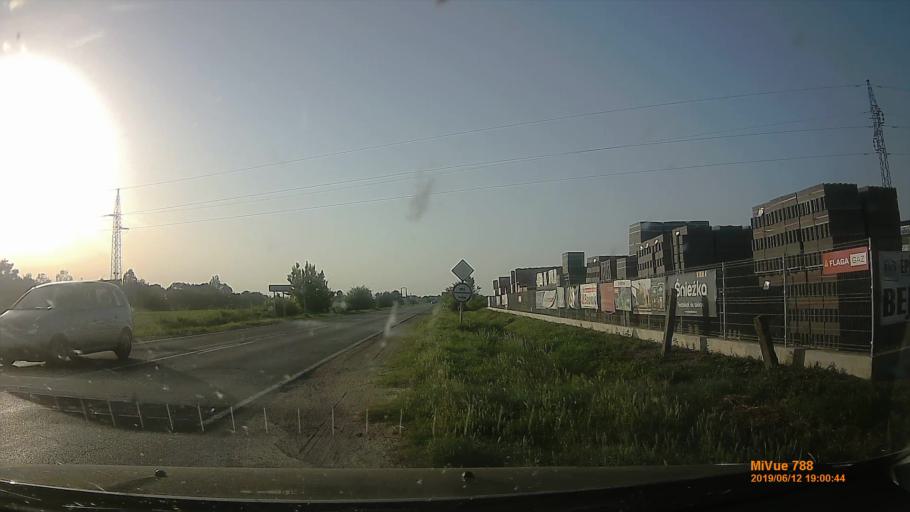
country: HU
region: Bacs-Kiskun
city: Kiskunfelegyhaza
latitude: 46.7308
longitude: 19.8448
